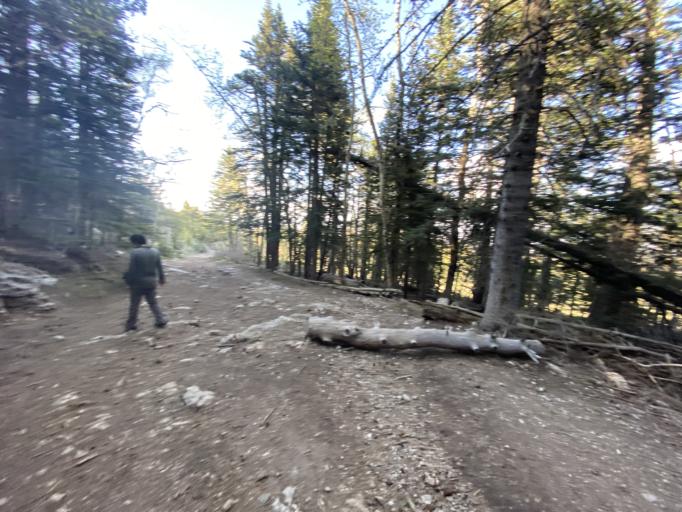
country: US
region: New Mexico
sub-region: Bernalillo County
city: Sandia Heights
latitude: 35.2055
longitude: -106.4437
